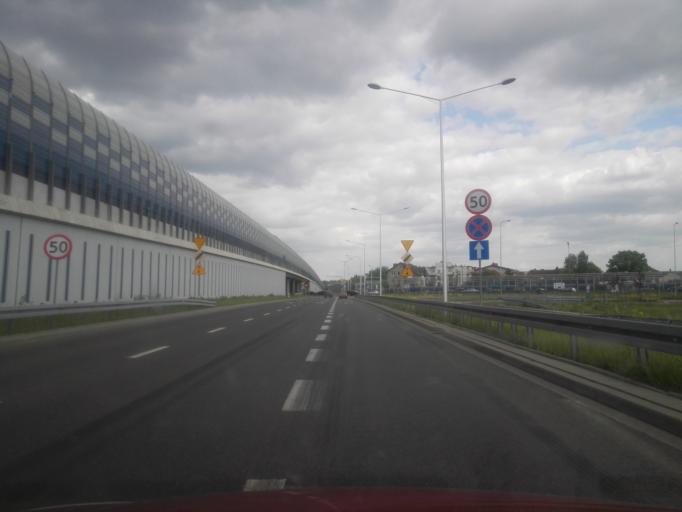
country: PL
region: Masovian Voivodeship
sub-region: Powiat wolominski
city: Marki
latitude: 52.3070
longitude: 21.0895
